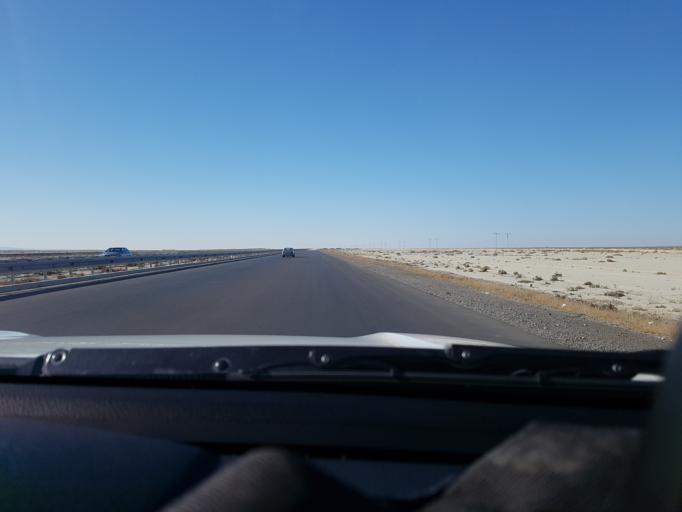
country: TM
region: Balkan
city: Gazanjyk
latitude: 39.2529
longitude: 55.1024
